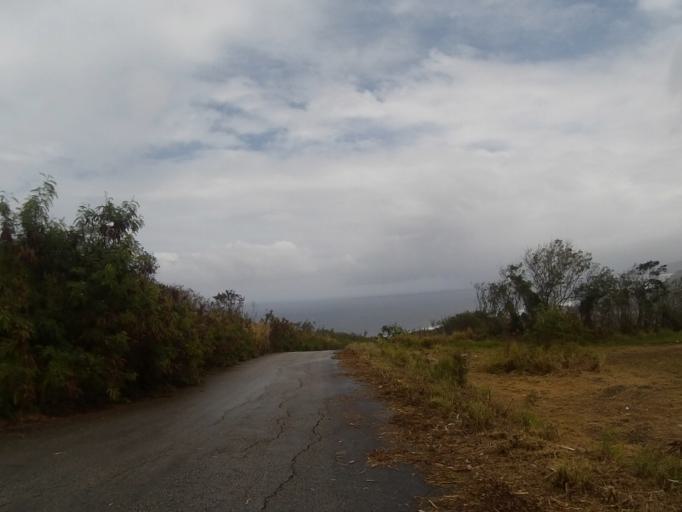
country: BB
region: Saint Andrew
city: Greenland
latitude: 13.2752
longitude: -59.5809
